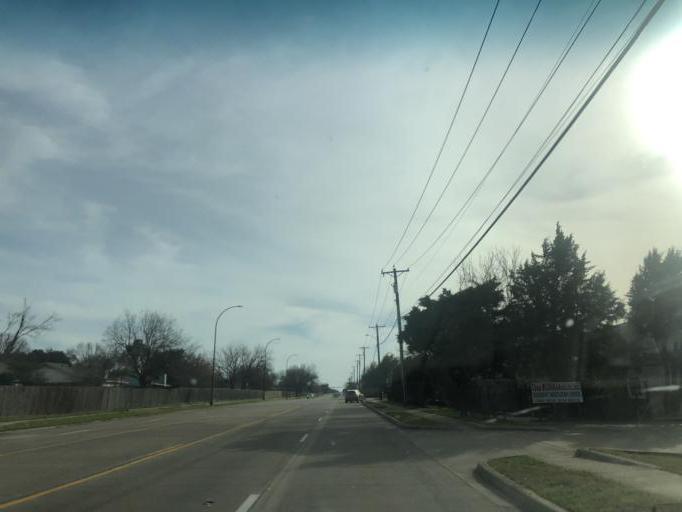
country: US
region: Texas
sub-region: Tarrant County
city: Dalworthington Gardens
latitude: 32.7039
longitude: -97.1492
